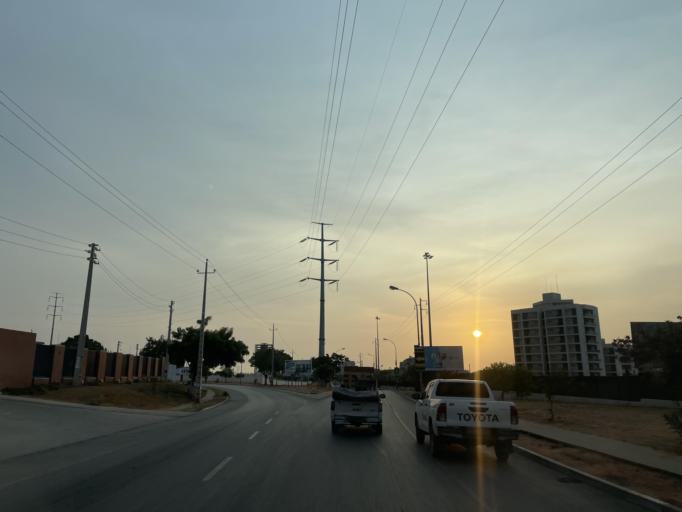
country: AO
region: Luanda
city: Luanda
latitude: -8.9143
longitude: 13.1944
